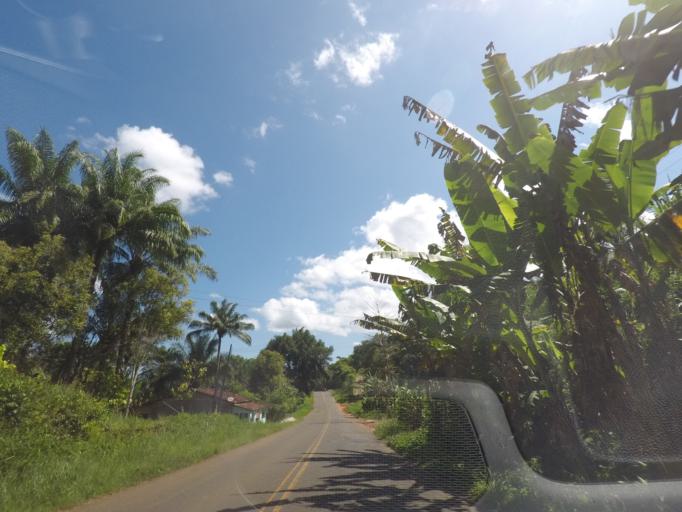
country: BR
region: Bahia
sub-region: Taperoa
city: Taperoa
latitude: -13.5755
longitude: -39.1062
